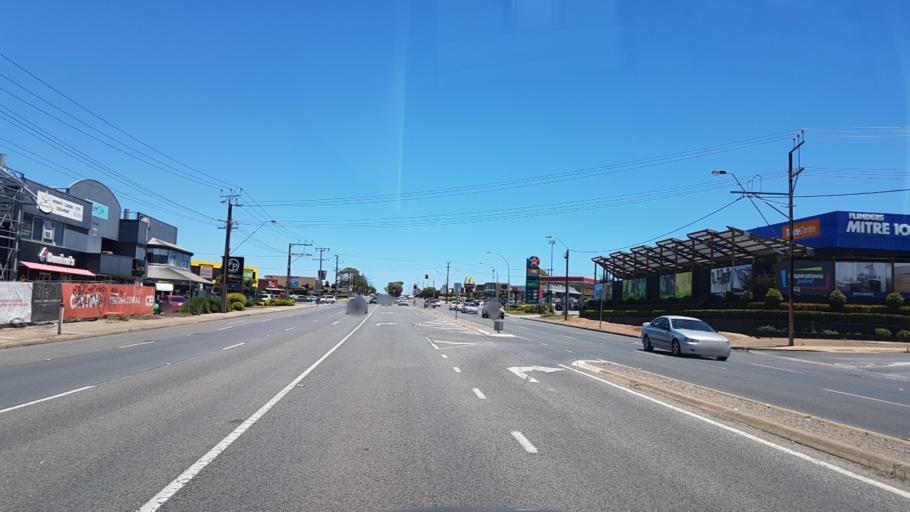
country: AU
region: South Australia
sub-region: Onkaparinga
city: Reynella
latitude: -35.1039
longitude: 138.5284
